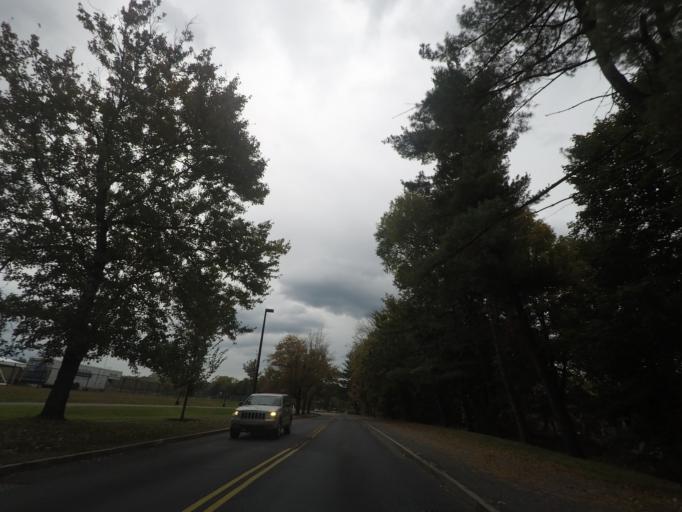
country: US
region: New York
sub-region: Albany County
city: McKownville
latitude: 42.6794
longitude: -73.8287
